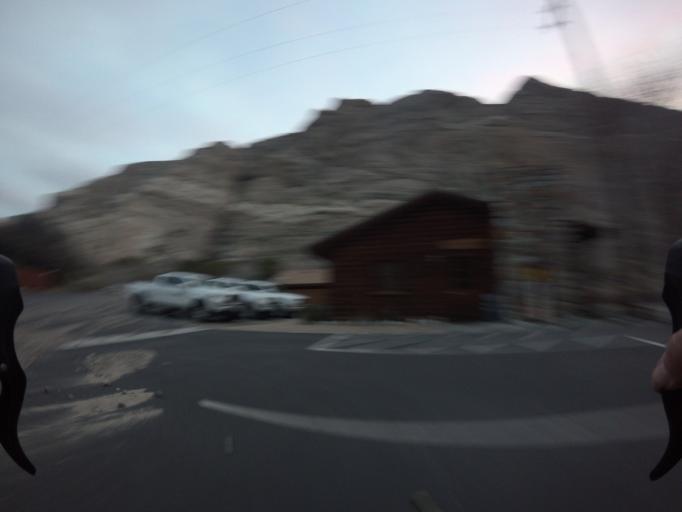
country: US
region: California
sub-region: San Bernardino County
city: Morongo Valley
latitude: 33.9890
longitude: -116.6558
